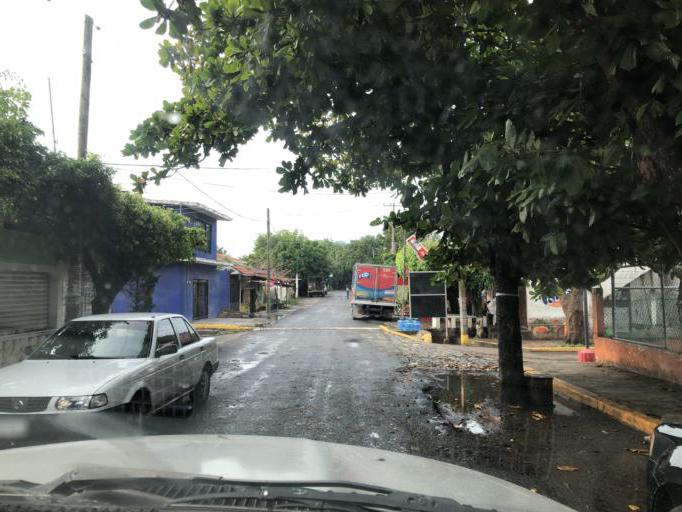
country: MX
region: Veracruz
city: Villa Emilio Carranza
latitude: 19.8902
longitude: -96.5070
